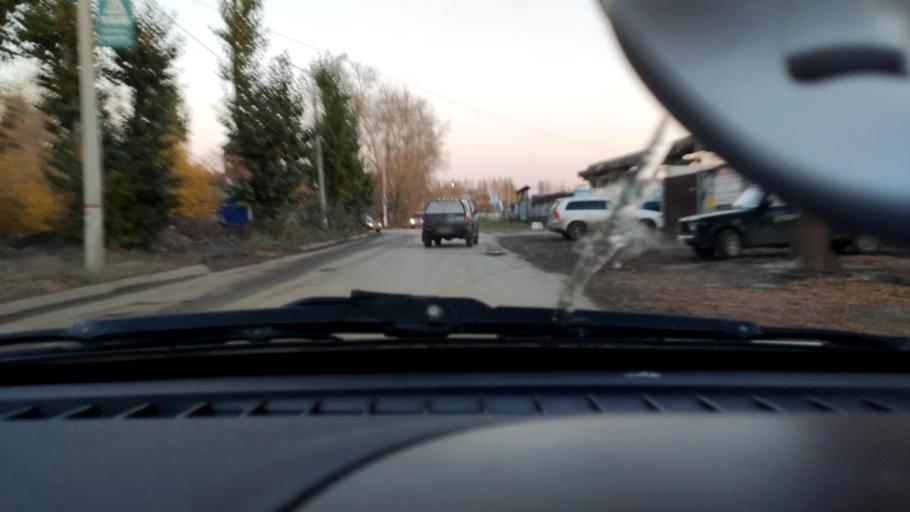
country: RU
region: Perm
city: Froly
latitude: 57.9659
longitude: 56.2685
